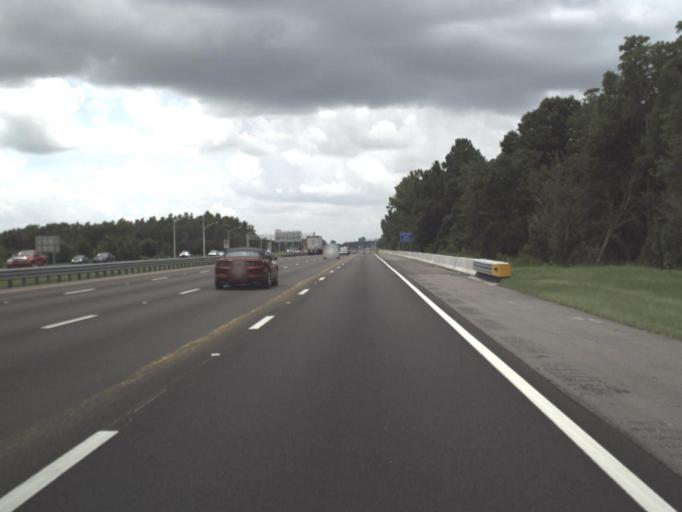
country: US
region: Florida
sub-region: Pasco County
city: Wesley Chapel
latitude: 28.2252
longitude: -82.3636
